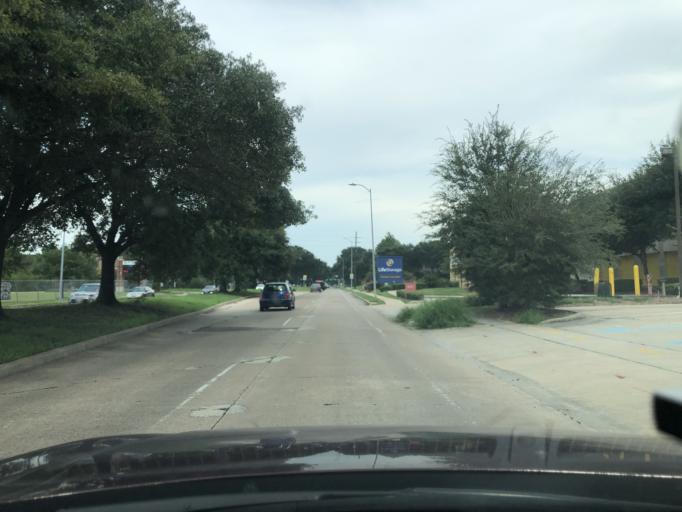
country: US
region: Texas
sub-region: Fort Bend County
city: Mission Bend
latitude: 29.7297
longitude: -95.6040
